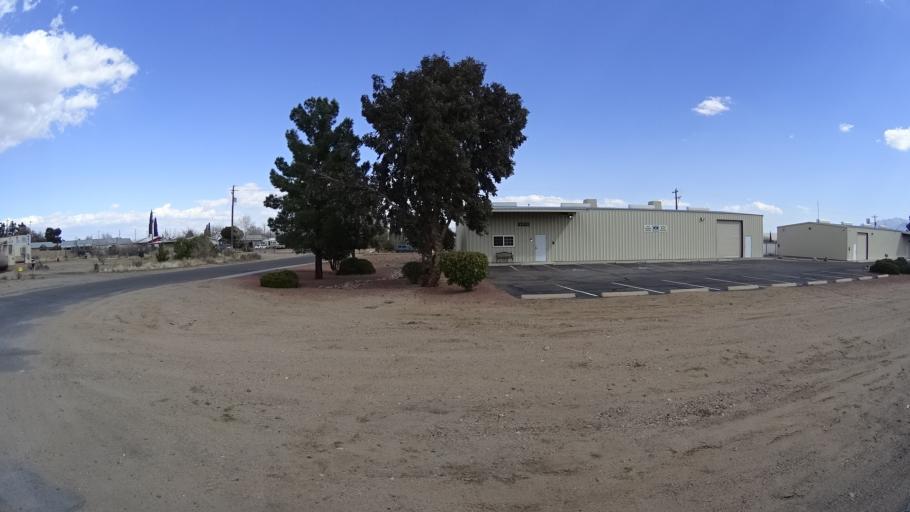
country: US
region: Arizona
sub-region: Mohave County
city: New Kingman-Butler
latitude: 35.2654
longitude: -114.0416
